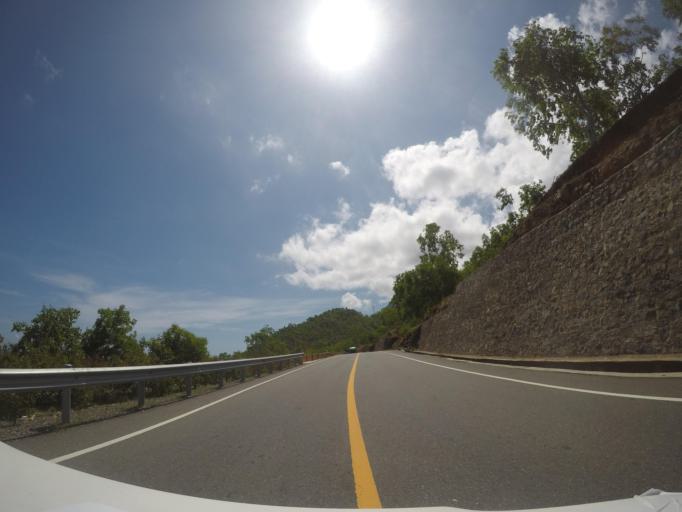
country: TL
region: Manatuto
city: Manatuto
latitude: -8.4762
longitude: 125.8946
